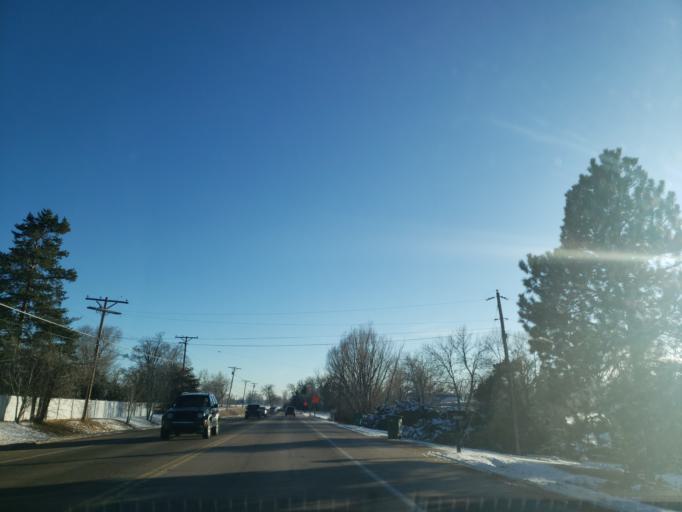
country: US
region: Colorado
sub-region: Larimer County
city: Fort Collins
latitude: 40.6235
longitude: -105.0718
